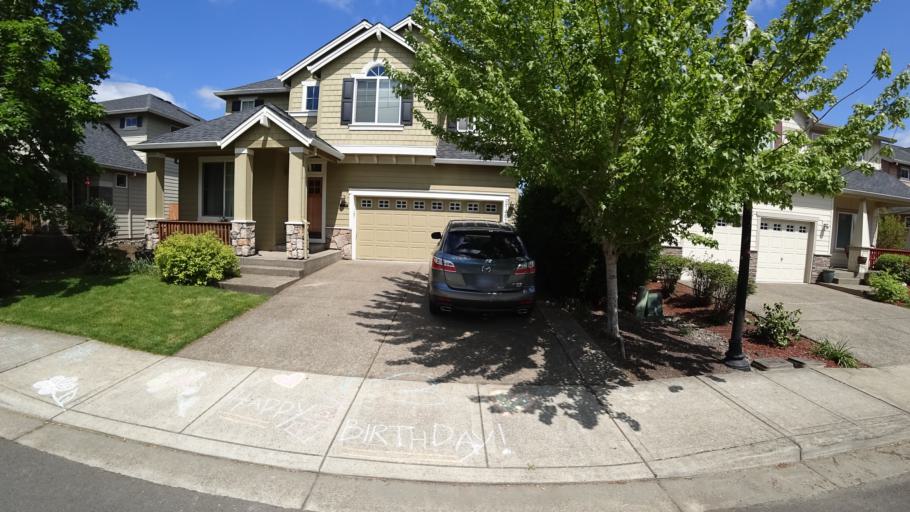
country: US
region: Oregon
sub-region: Washington County
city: Aloha
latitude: 45.5088
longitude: -122.8982
